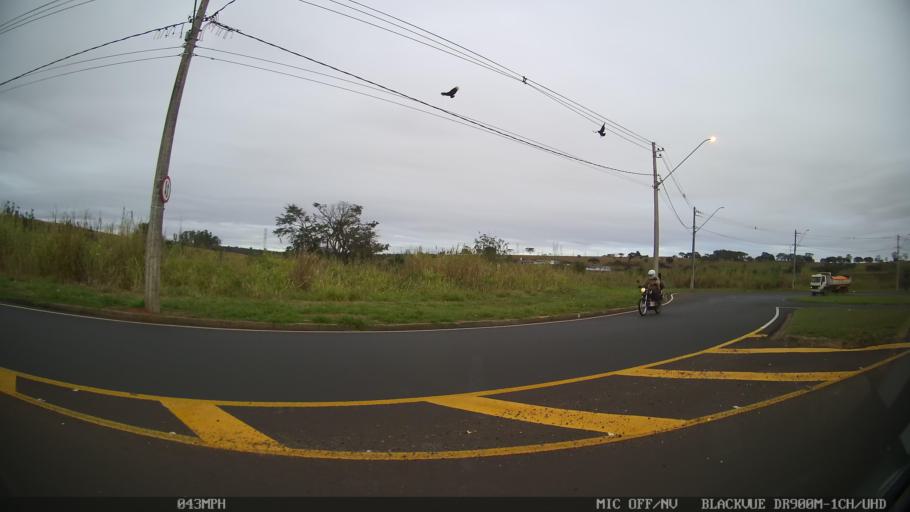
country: BR
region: Sao Paulo
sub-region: Sao Jose Do Rio Preto
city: Sao Jose do Rio Preto
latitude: -20.8233
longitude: -49.4365
